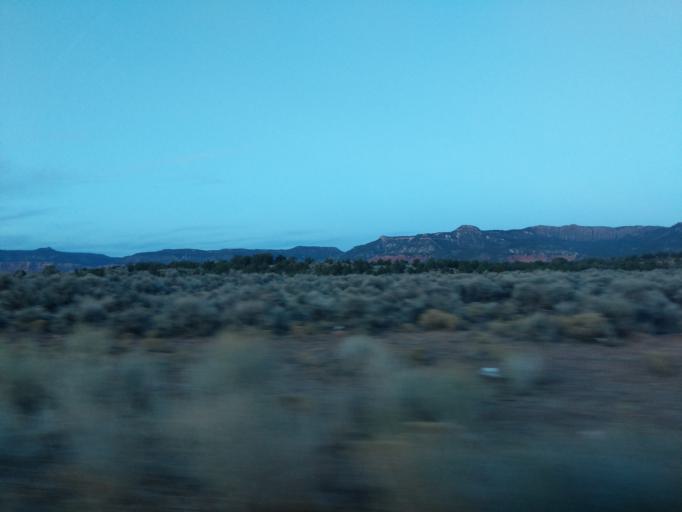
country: US
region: Arizona
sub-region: Apache County
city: Tsaile
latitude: 36.3435
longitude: -109.2393
